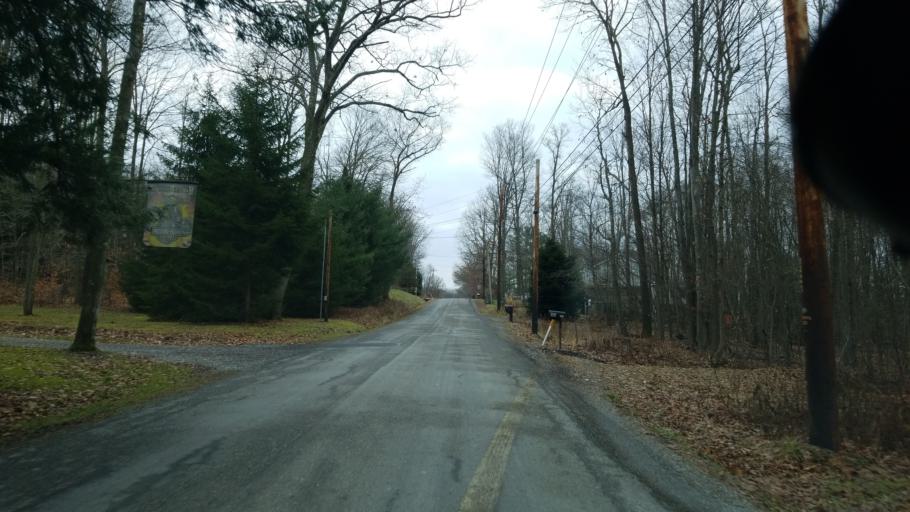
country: US
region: Pennsylvania
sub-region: Clearfield County
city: Treasure Lake
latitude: 41.1131
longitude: -78.6919
